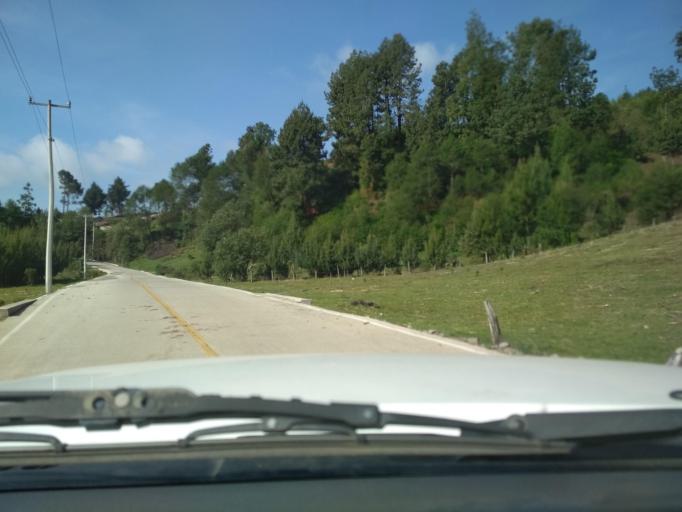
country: MX
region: Veracruz
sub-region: La Perla
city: Chilapa
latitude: 19.0055
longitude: -97.1822
